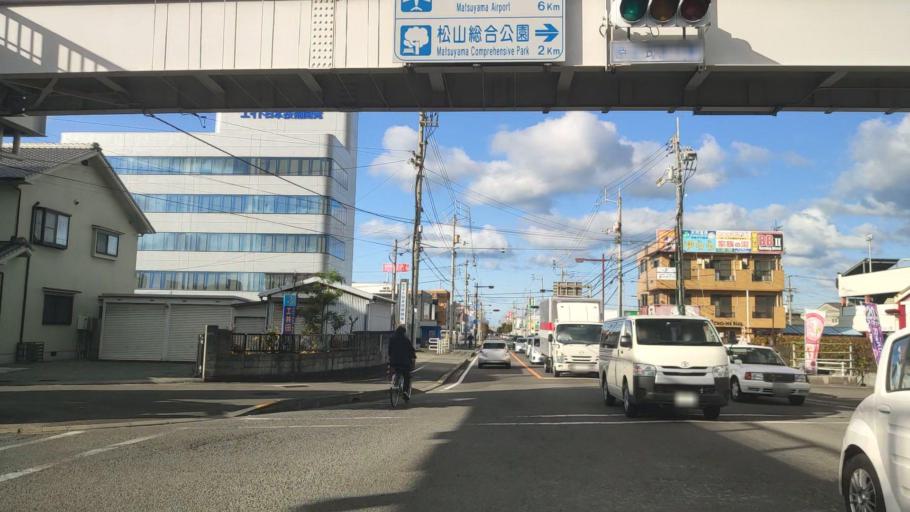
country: JP
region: Ehime
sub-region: Shikoku-chuo Shi
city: Matsuyama
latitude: 33.8285
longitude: 132.7442
